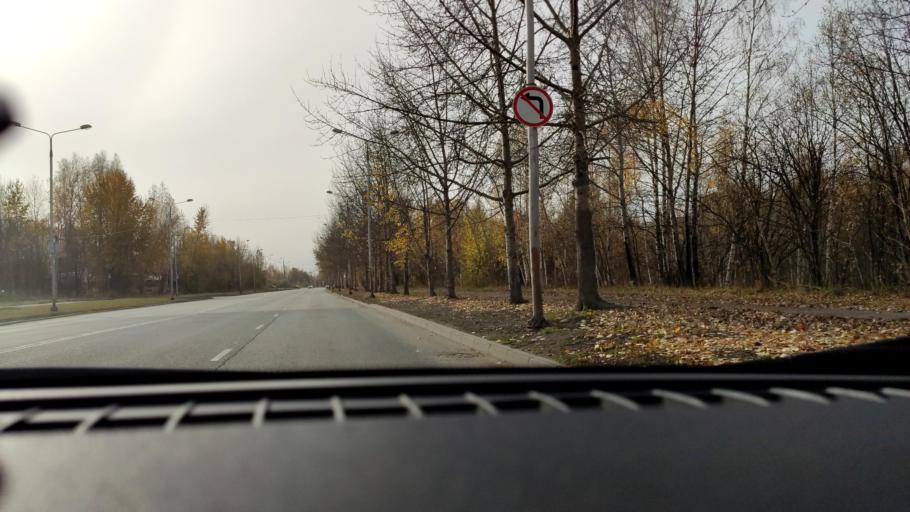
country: RU
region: Perm
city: Perm
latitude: 58.1040
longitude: 56.3925
